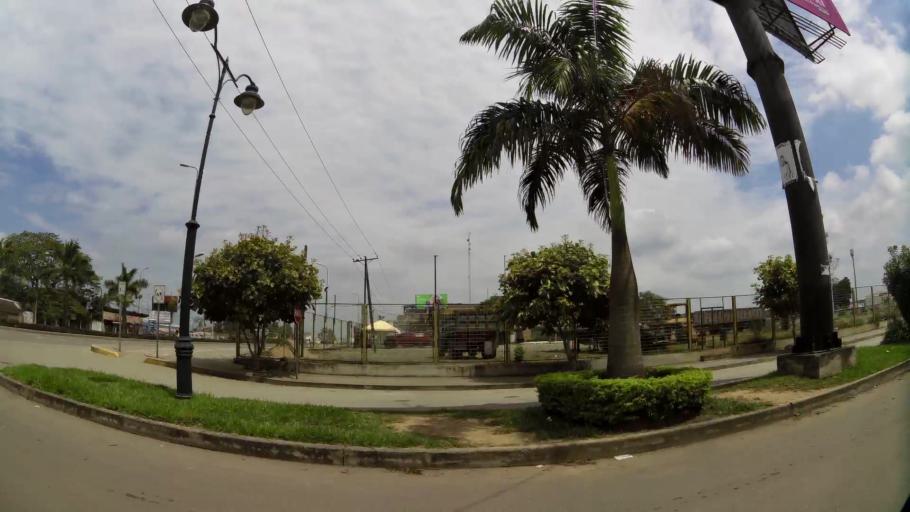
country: EC
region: El Oro
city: Machala
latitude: -3.2809
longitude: -79.9307
